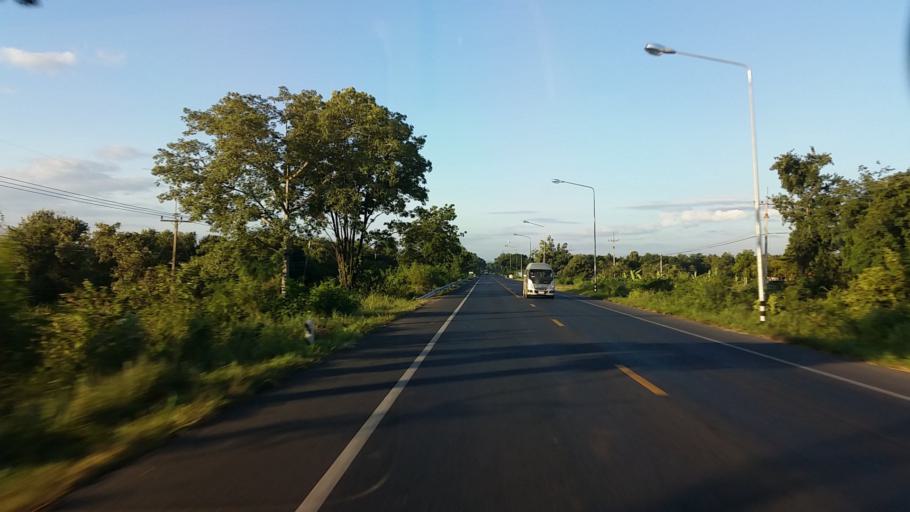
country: TH
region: Lop Buri
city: Chai Badan
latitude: 15.2621
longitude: 101.1895
